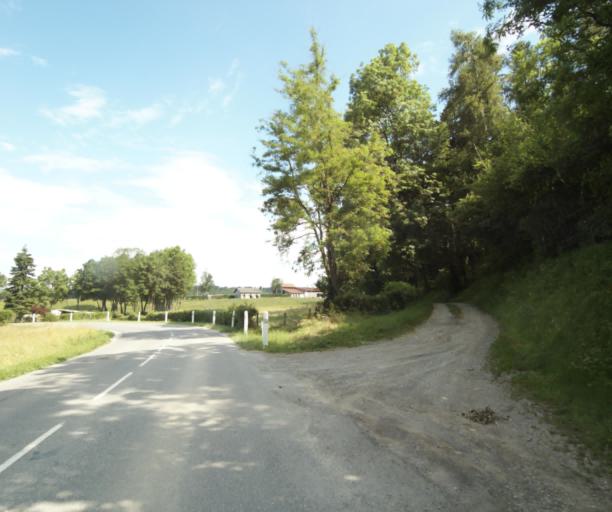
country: FR
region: Rhone-Alpes
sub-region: Departement de la Haute-Savoie
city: Armoy
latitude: 46.3343
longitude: 6.4962
